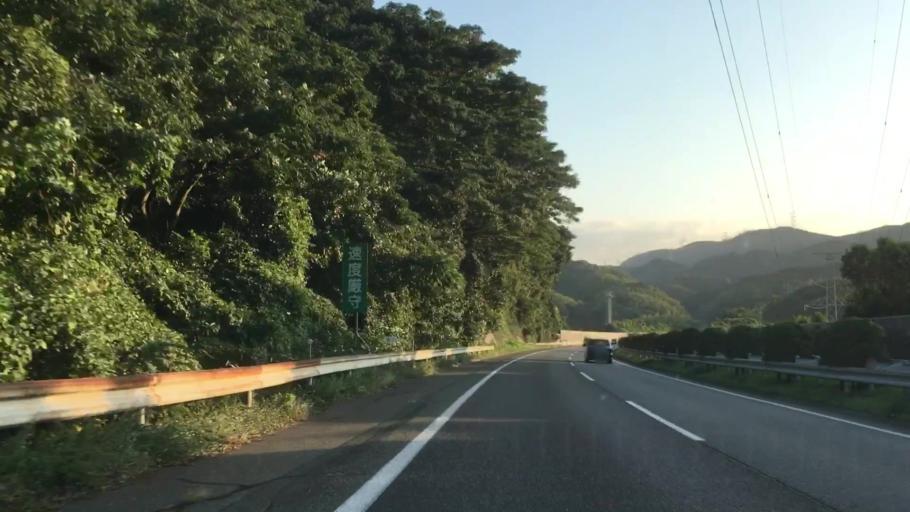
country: JP
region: Yamaguchi
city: Shimonoseki
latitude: 33.9111
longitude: 130.9754
